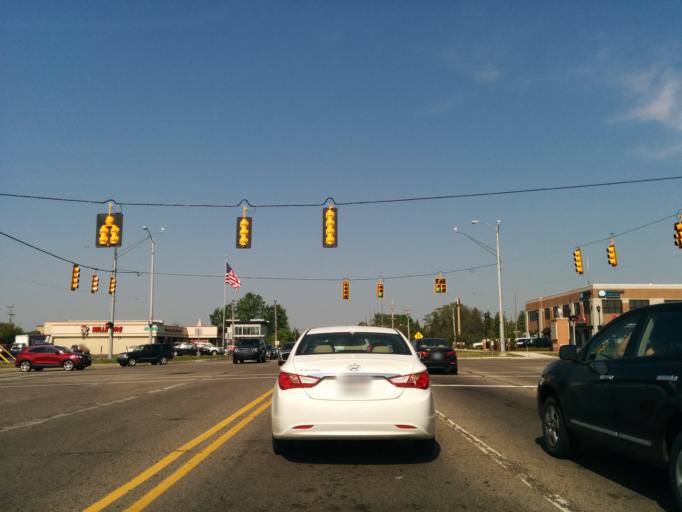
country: US
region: Michigan
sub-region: Oakland County
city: West Bloomfield Township
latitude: 42.5430
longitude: -83.3602
